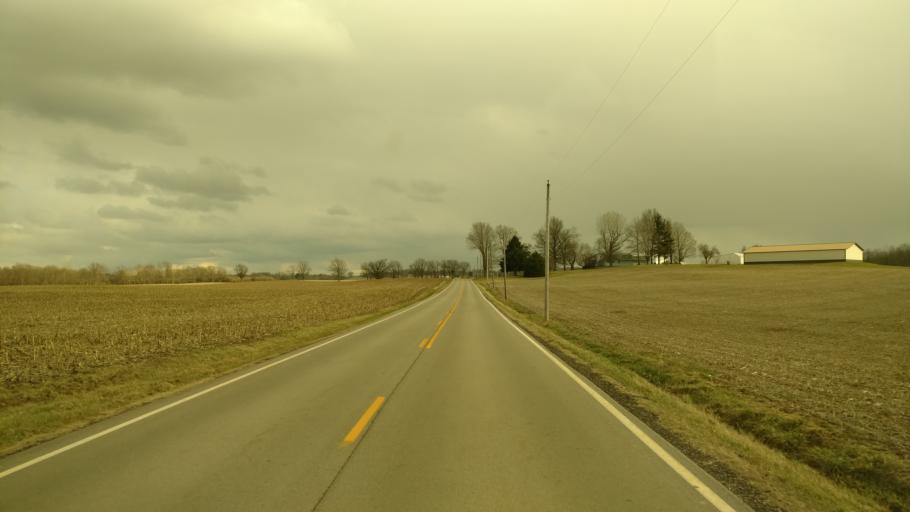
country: US
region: Ohio
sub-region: Crawford County
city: Galion
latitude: 40.7229
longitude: -82.7368
